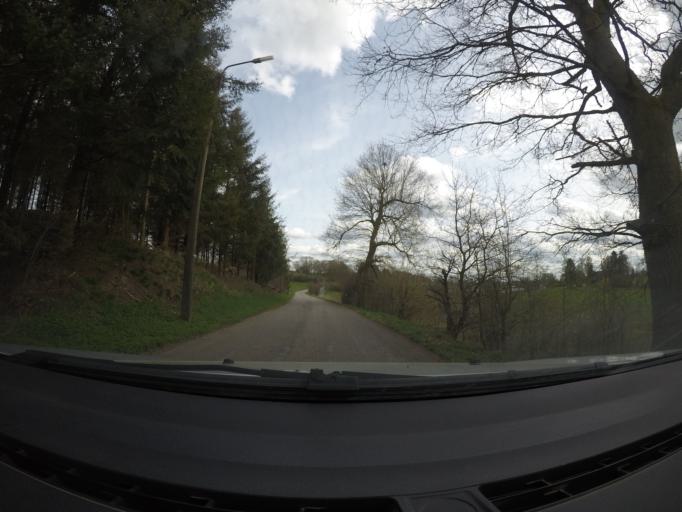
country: BE
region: Wallonia
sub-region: Province du Luxembourg
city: Neufchateau
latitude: 49.8137
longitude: 5.4783
